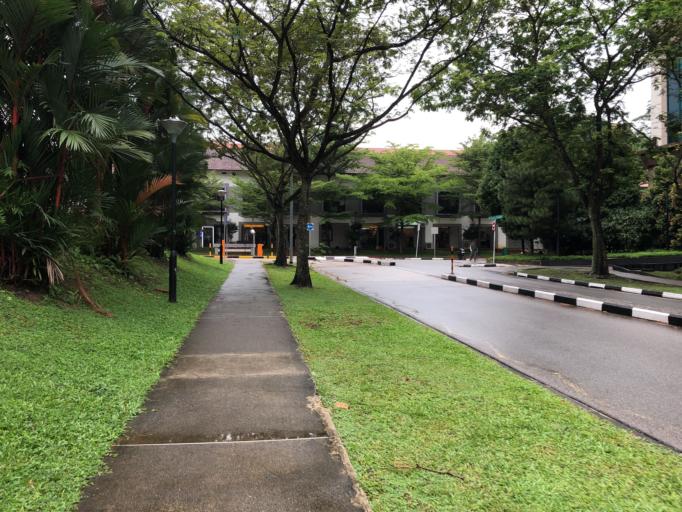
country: MY
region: Johor
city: Johor Bahru
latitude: 1.3506
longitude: 103.7494
